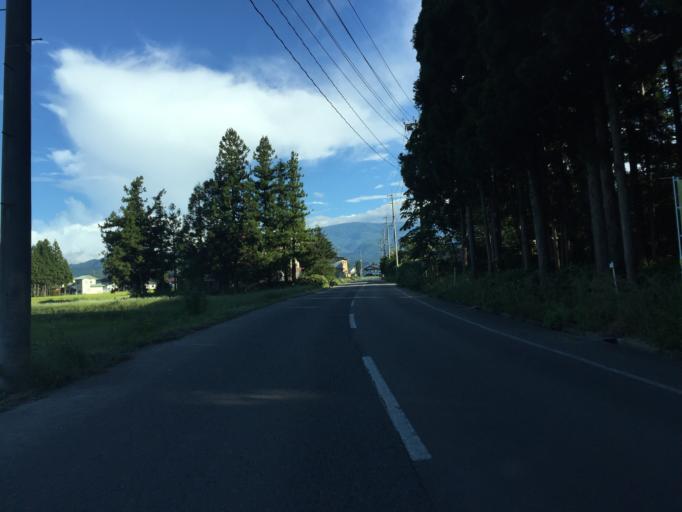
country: JP
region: Yamagata
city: Yonezawa
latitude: 37.8837
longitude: 140.0967
